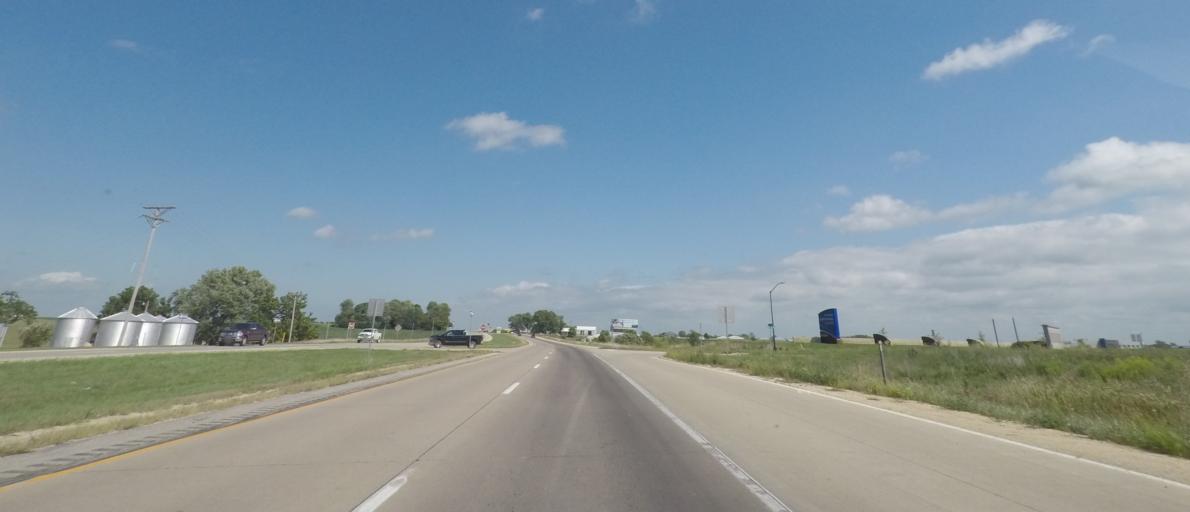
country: US
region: Iowa
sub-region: Linn County
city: Marion
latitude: 42.0355
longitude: -91.5411
